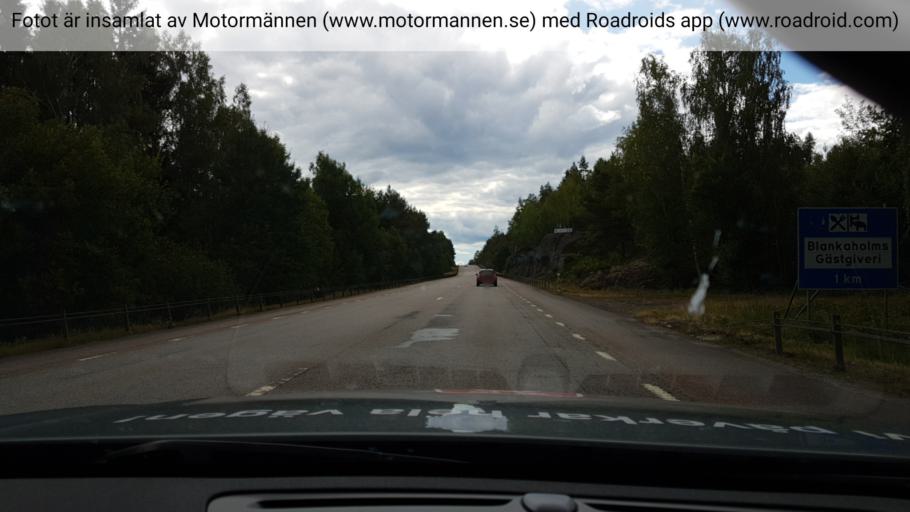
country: SE
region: Kalmar
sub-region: Vasterviks Kommun
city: Ankarsrum
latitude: 57.5988
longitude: 16.4813
